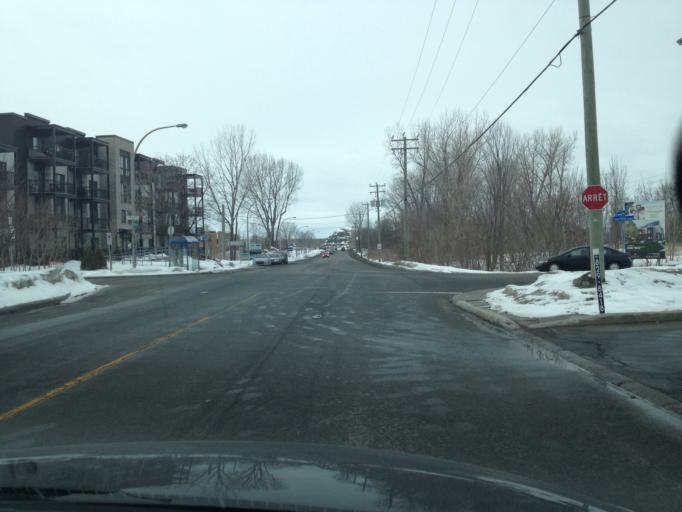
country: CA
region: Quebec
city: Dollard-Des Ormeaux
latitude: 45.5414
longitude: -73.7886
